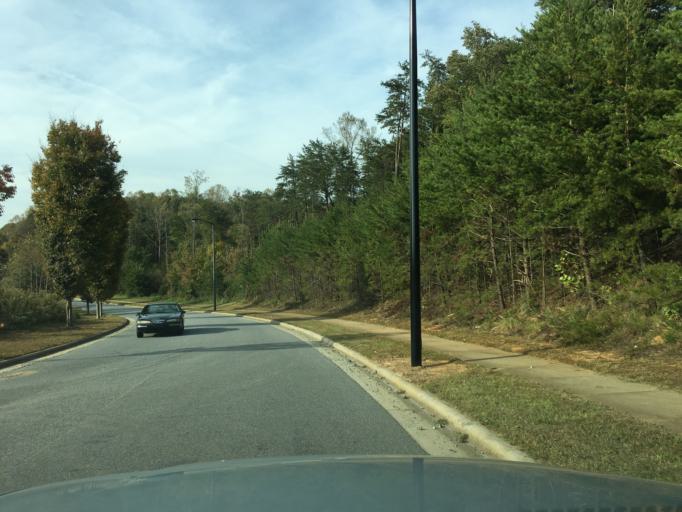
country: US
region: North Carolina
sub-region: Catawba County
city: Saint Stephens
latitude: 35.7296
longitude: -81.2871
